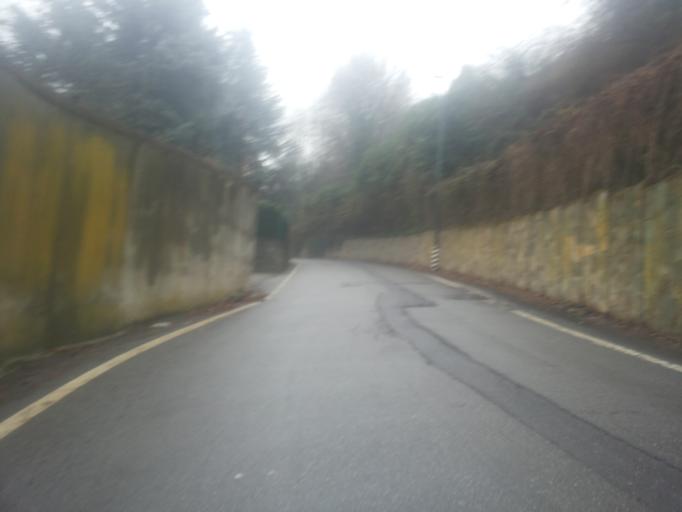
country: IT
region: Piedmont
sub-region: Provincia di Torino
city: Turin
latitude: 45.0505
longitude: 7.7076
